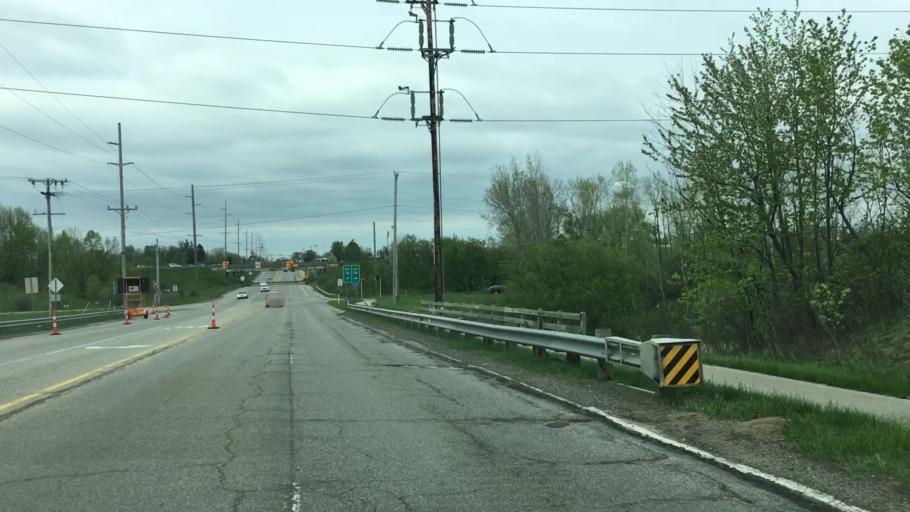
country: US
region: Michigan
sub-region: Ottawa County
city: Hudsonville
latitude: 42.8457
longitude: -85.8615
